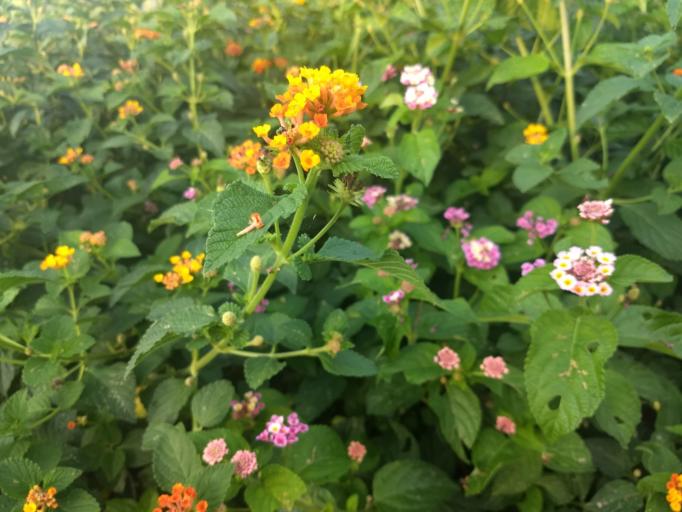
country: MX
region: Nuevo Leon
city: Guadalupe
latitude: 25.6764
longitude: -100.2870
